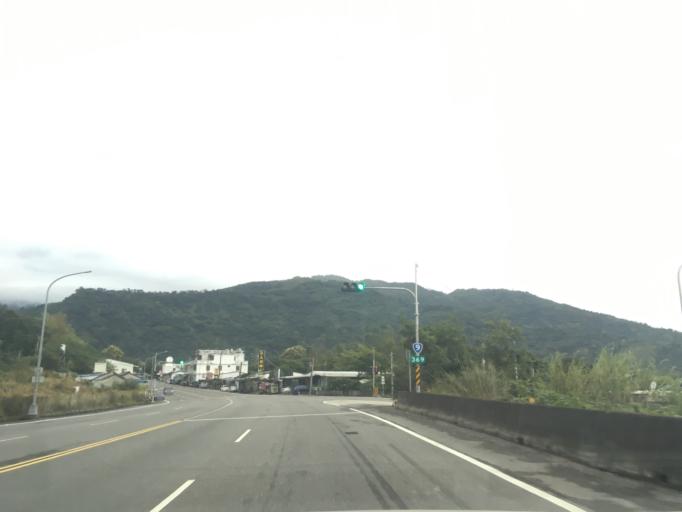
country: TW
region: Taiwan
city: Taitung City
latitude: 22.7559
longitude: 121.0530
